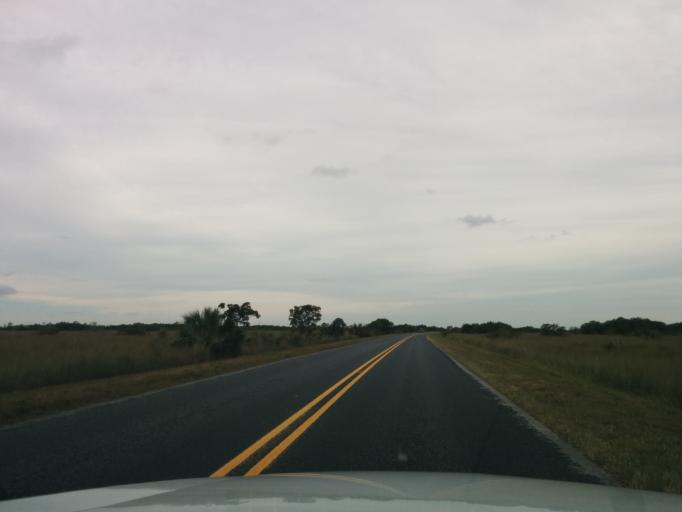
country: US
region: Florida
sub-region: Miami-Dade County
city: Florida City
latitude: 25.4329
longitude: -80.7353
